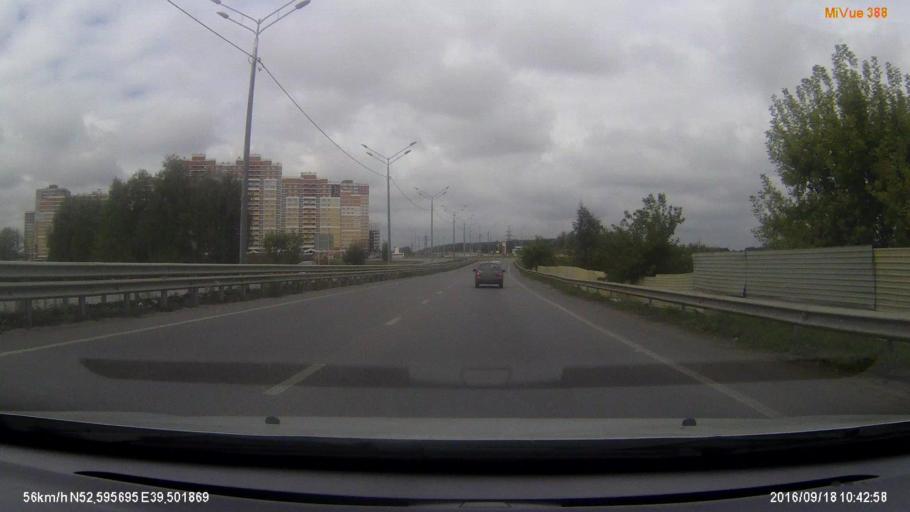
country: RU
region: Lipetsk
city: Syrskoye
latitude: 52.5955
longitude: 39.5020
